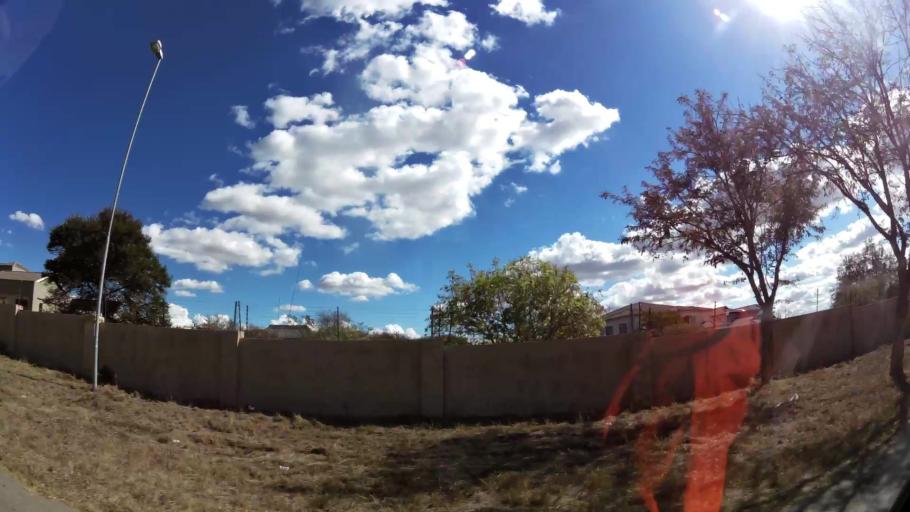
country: ZA
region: Limpopo
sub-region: Capricorn District Municipality
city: Polokwane
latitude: -23.8604
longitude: 29.5099
